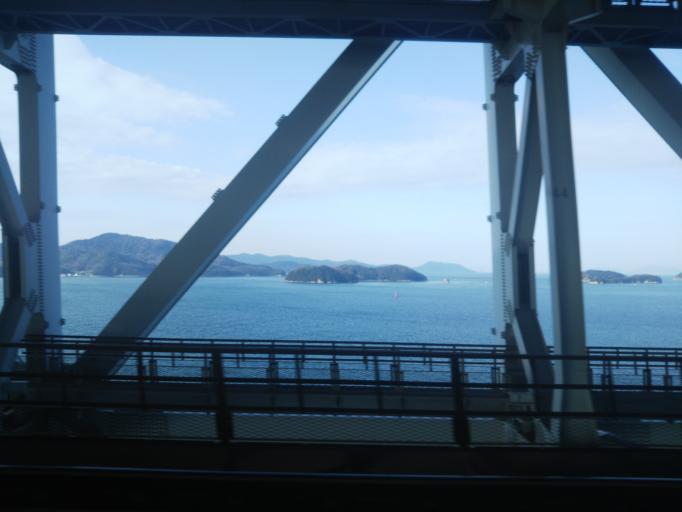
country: JP
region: Kagawa
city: Sakaidecho
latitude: 34.4083
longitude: 133.8073
